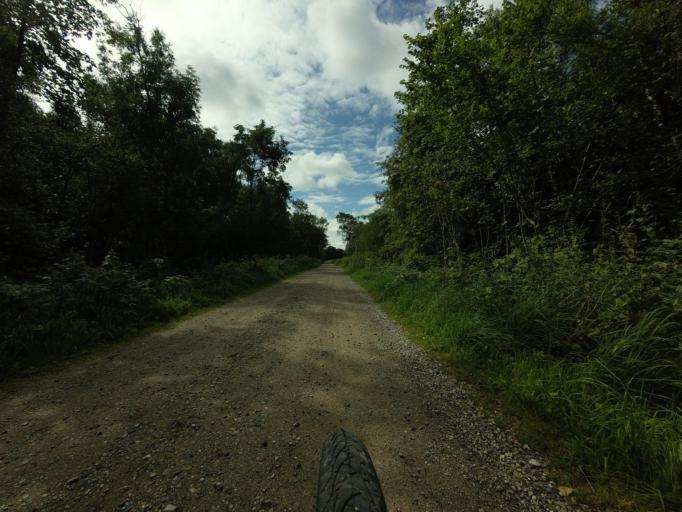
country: DK
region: Central Jutland
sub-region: Norddjurs Kommune
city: Auning
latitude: 56.4404
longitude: 10.3666
